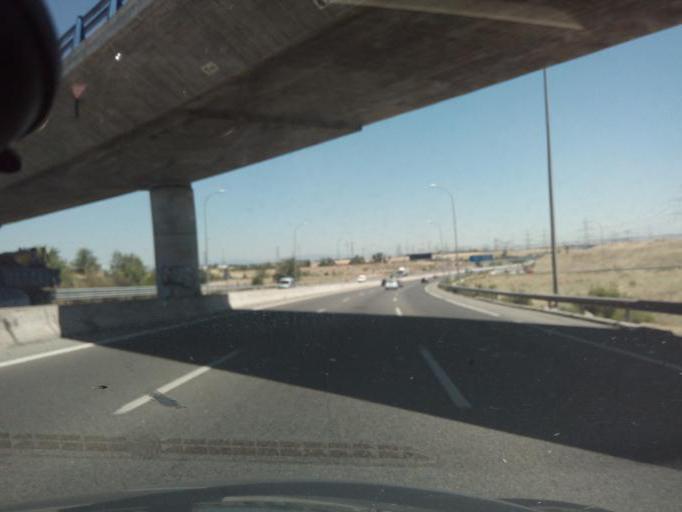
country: ES
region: Madrid
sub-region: Provincia de Madrid
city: San Sebastian de los Reyes
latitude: 40.5527
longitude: -3.6071
